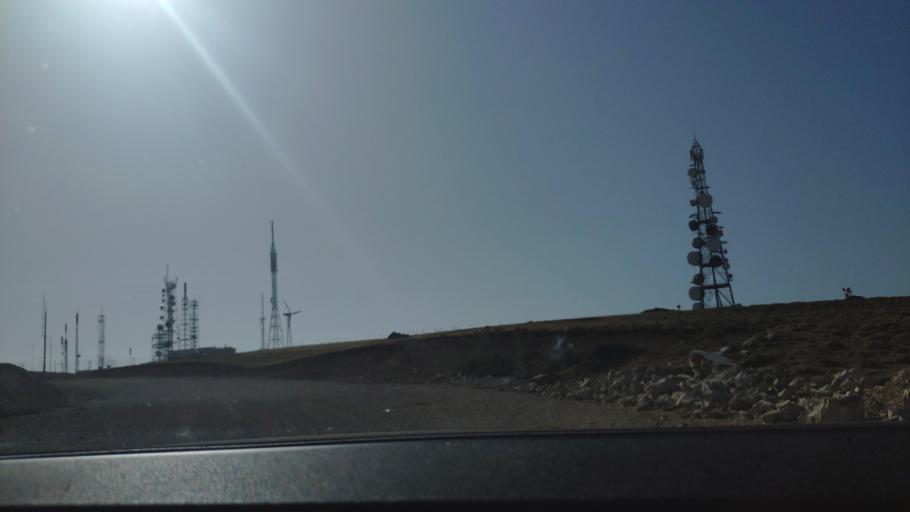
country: GR
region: West Greece
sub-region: Nomos Aitolias kai Akarnanias
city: Monastirakion
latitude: 38.8080
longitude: 20.9807
